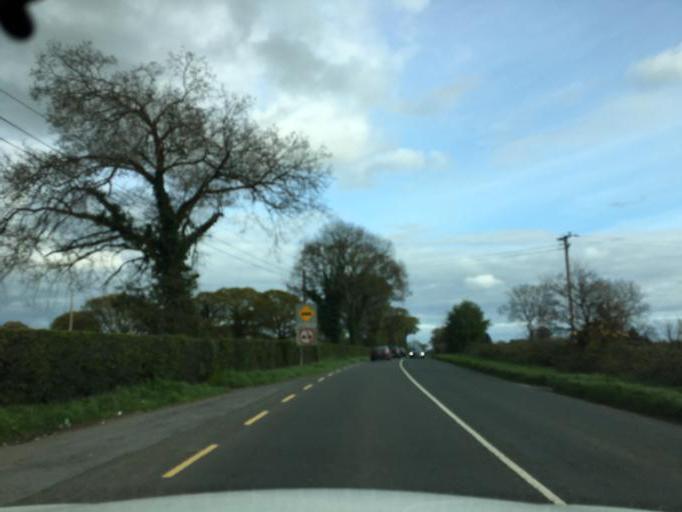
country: IE
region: Leinster
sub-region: Loch Garman
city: New Ross
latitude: 52.4327
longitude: -6.9544
